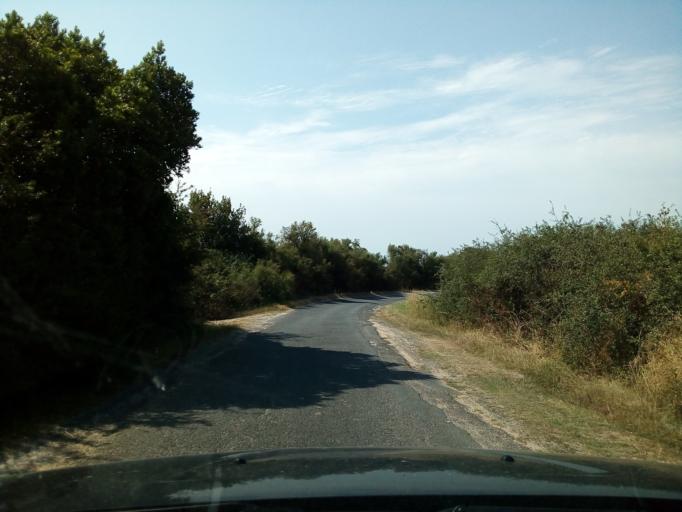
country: FR
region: Poitou-Charentes
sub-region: Departement de la Charente-Maritime
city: Boyard-Ville
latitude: 45.9564
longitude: -1.2623
